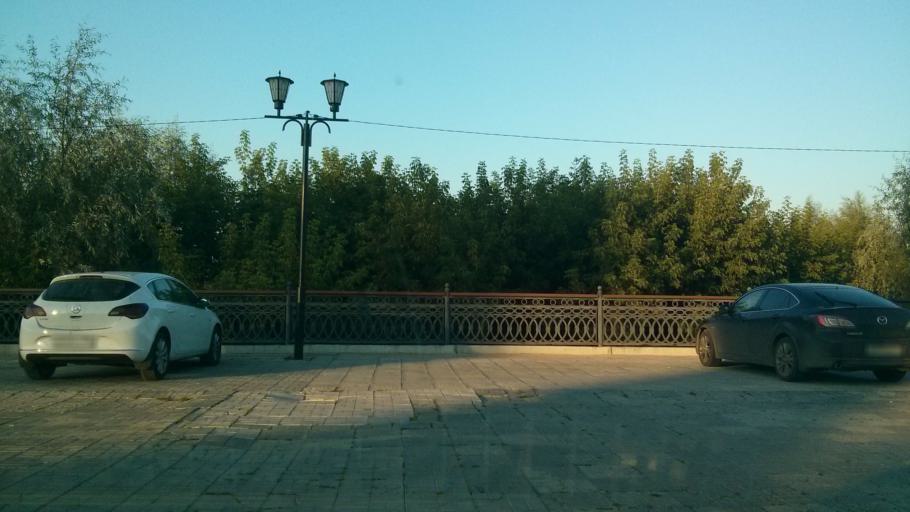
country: RU
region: Vladimir
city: Murom
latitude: 55.5806
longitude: 42.0627
